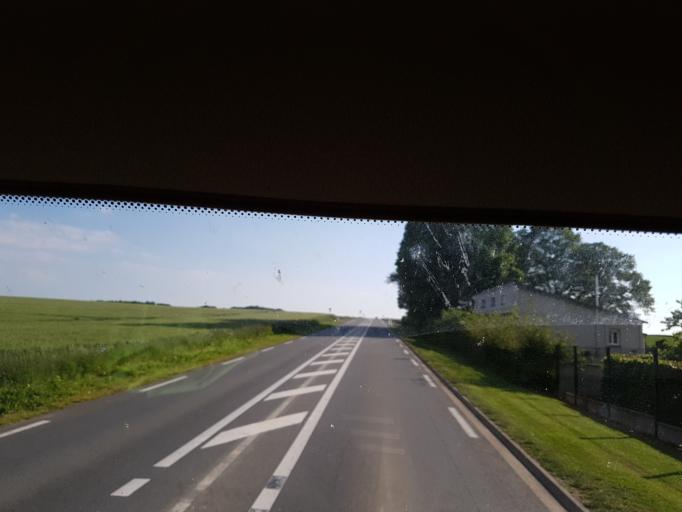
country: FR
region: Picardie
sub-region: Departement de la Somme
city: Crecy-en-Ponthieu
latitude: 50.2240
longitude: 1.9265
